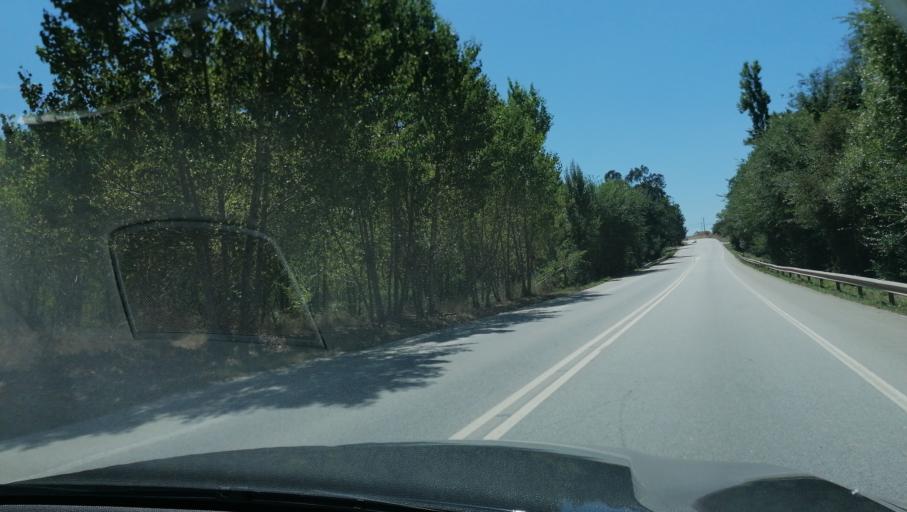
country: PT
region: Aveiro
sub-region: Agueda
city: Aguada de Cima
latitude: 40.5156
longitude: -8.4493
